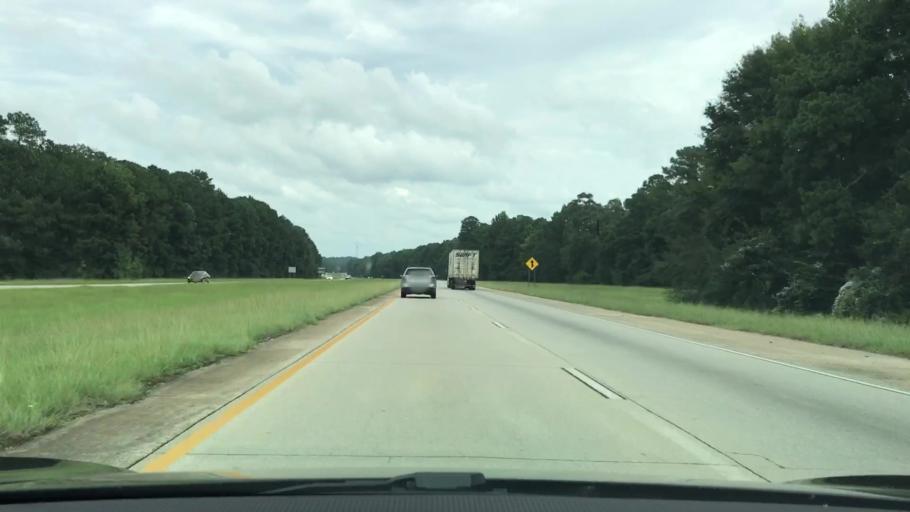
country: US
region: Georgia
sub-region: Troup County
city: La Grange
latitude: 33.0010
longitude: -85.0107
